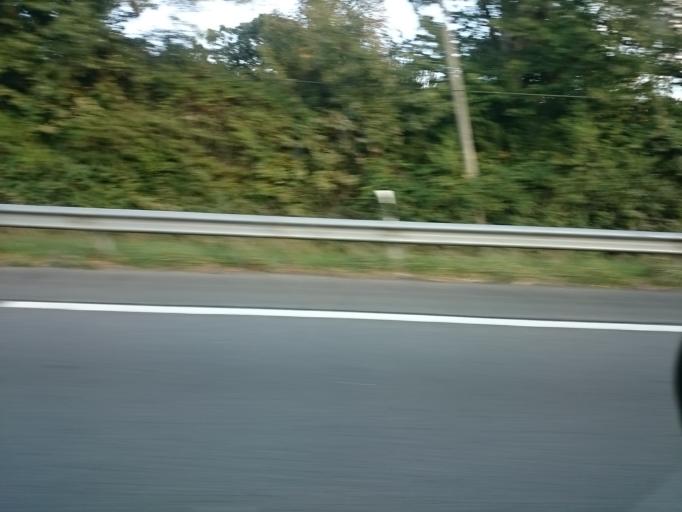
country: FR
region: Pays de la Loire
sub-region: Departement de la Loire-Atlantique
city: Heric
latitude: 47.4098
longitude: -1.6417
